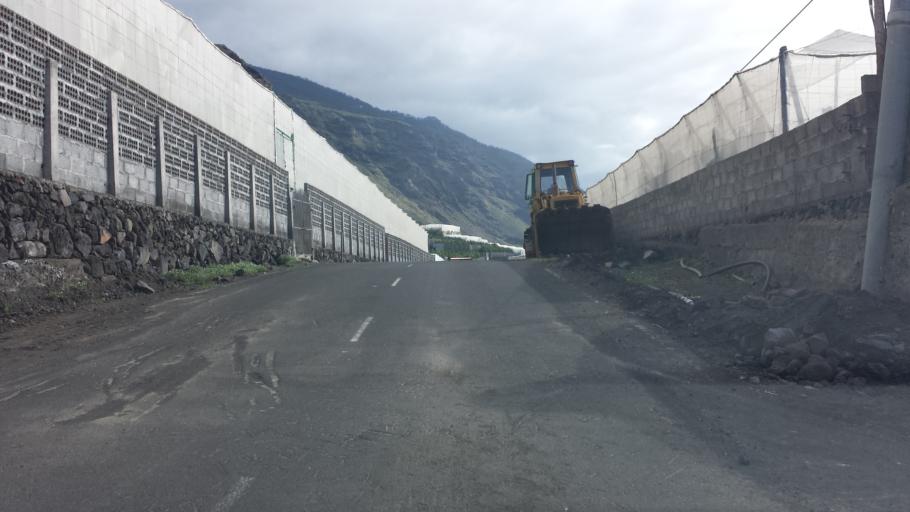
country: ES
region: Canary Islands
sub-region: Provincia de Santa Cruz de Tenerife
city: El Paso
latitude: 28.5682
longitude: -17.8943
